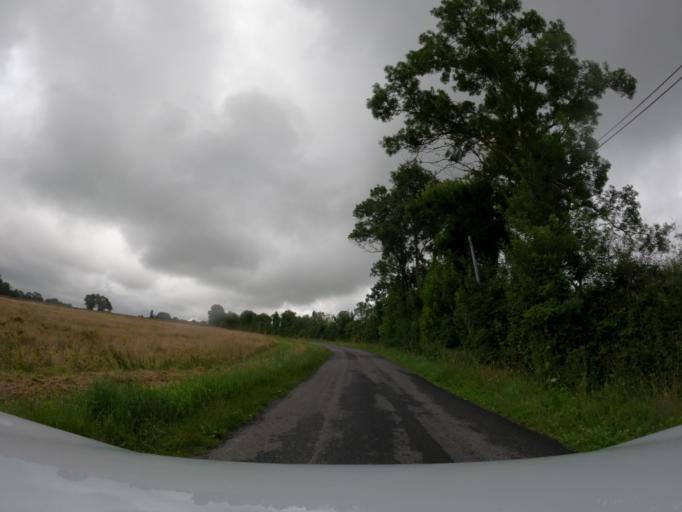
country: FR
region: Pays de la Loire
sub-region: Departement de la Loire-Atlantique
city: Saint-Mars-du-Desert
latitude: 47.3829
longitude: -1.4177
